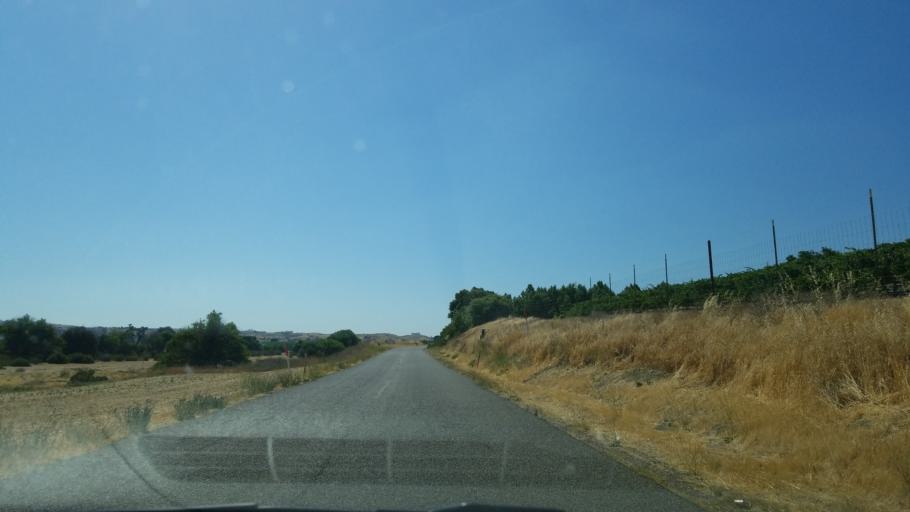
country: US
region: California
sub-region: San Luis Obispo County
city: San Miguel
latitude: 35.7327
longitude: -120.6634
